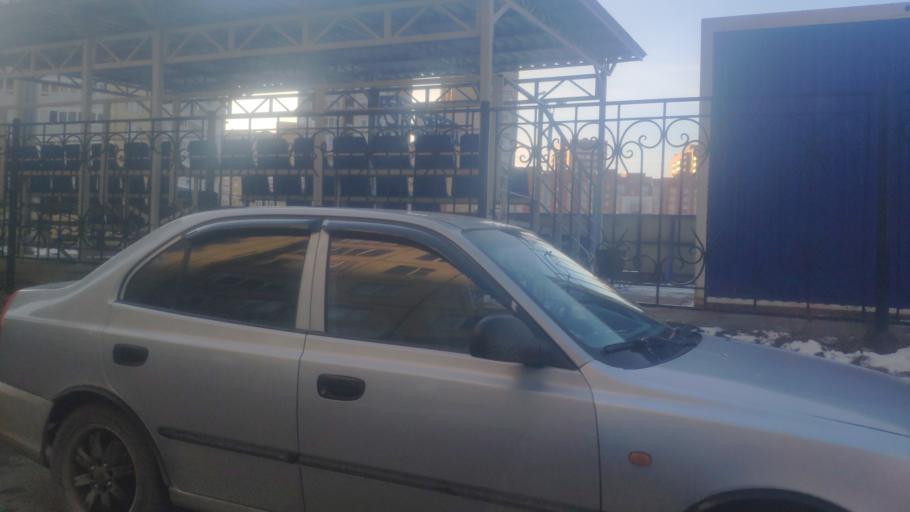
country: RU
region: Tjumen
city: Tyumen
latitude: 57.1770
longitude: 65.5657
